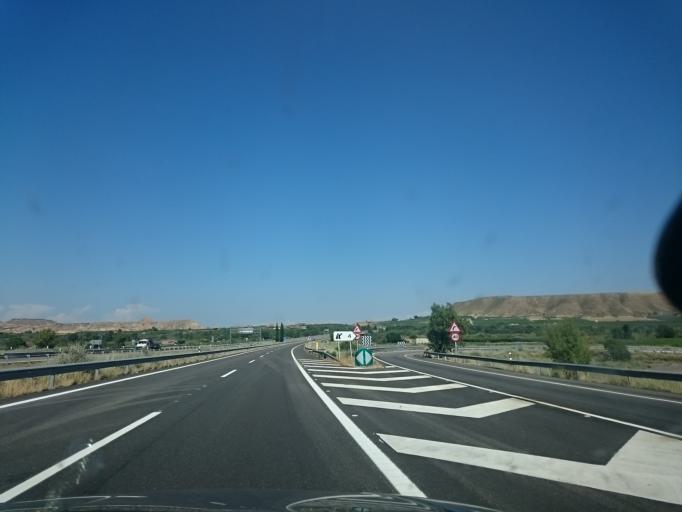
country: ES
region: Aragon
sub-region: Provincia de Huesca
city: Fraga
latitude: 41.4900
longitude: 0.3390
